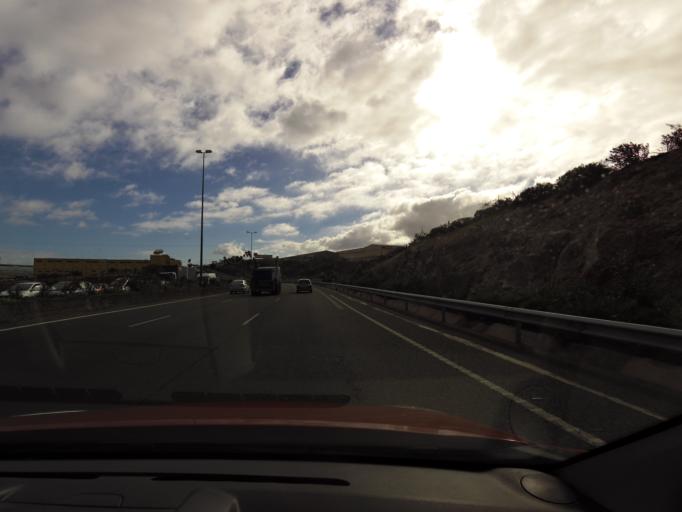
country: ES
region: Canary Islands
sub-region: Provincia de Las Palmas
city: Telde
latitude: 27.9766
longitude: -15.3911
